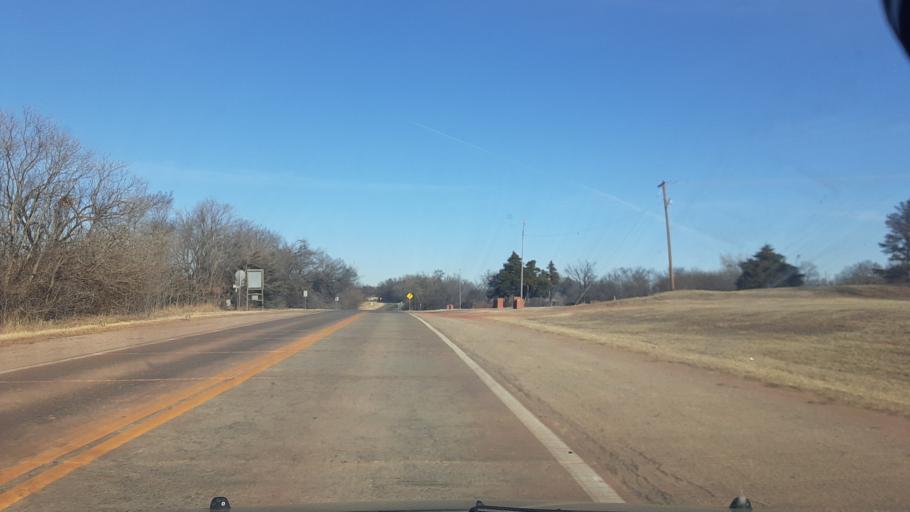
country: US
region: Oklahoma
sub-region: Logan County
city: Guthrie
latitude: 35.8919
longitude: -97.4240
